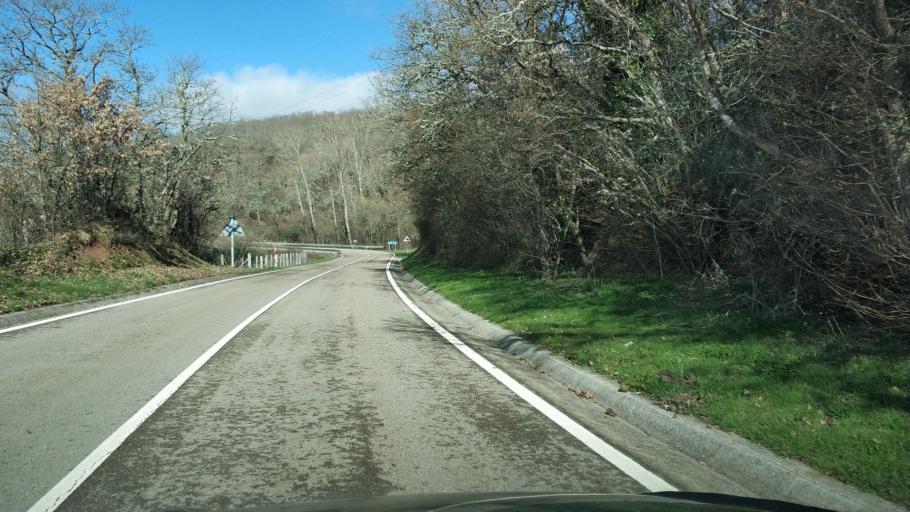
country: ES
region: Cantabria
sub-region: Provincia de Cantabria
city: Mataporquera
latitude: 42.9071
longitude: -4.0610
